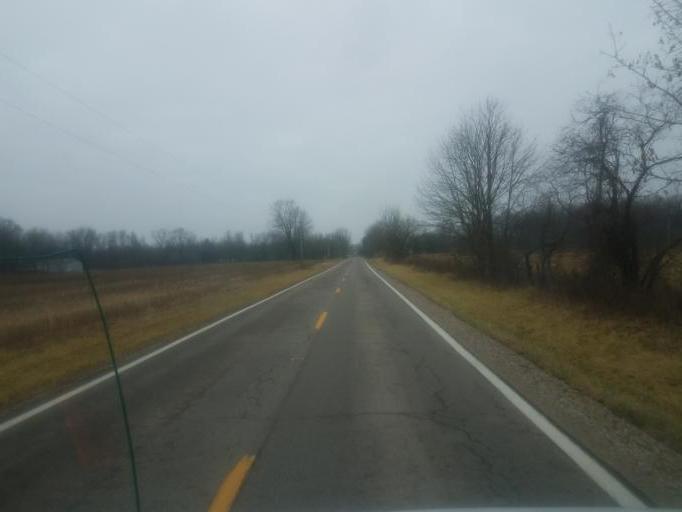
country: US
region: Ohio
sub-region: Knox County
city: Centerburg
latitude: 40.3505
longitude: -82.7768
